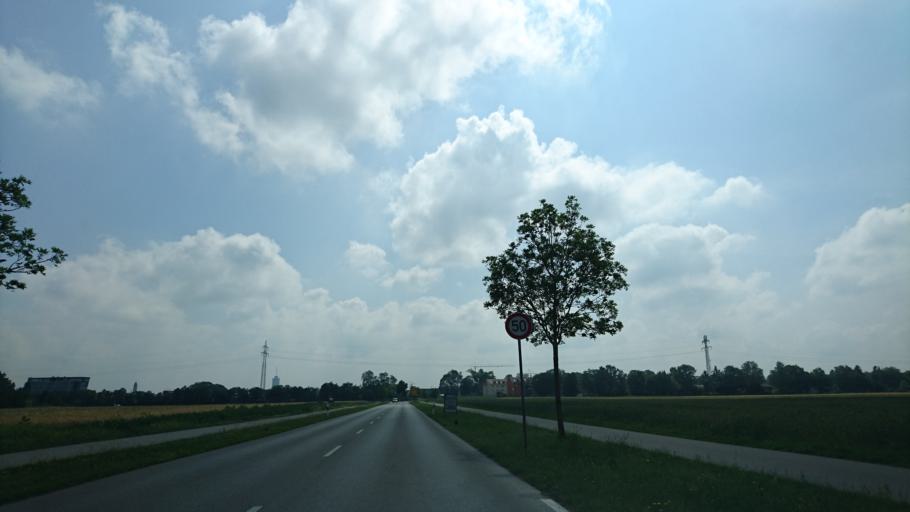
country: DE
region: Bavaria
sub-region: Swabia
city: Stadtbergen
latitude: 48.3581
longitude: 10.8443
